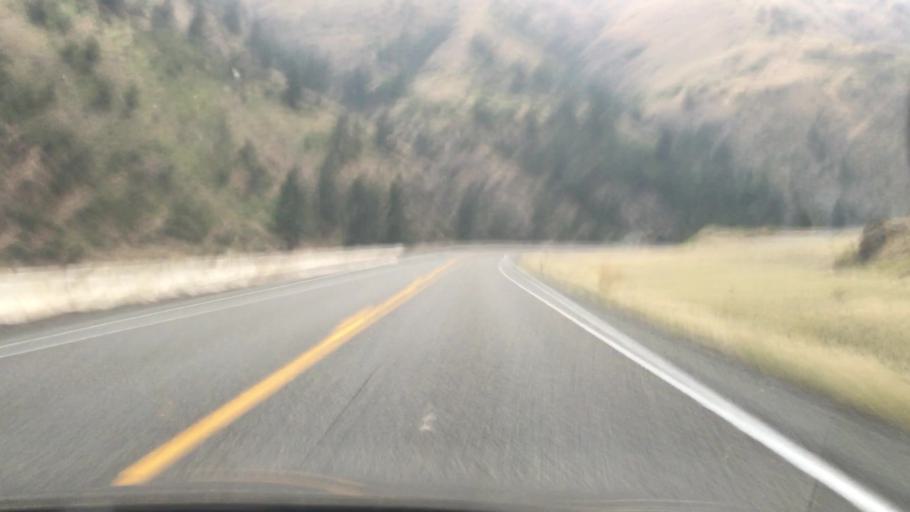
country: US
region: Idaho
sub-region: Idaho County
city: Grangeville
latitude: 45.6221
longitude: -116.2988
